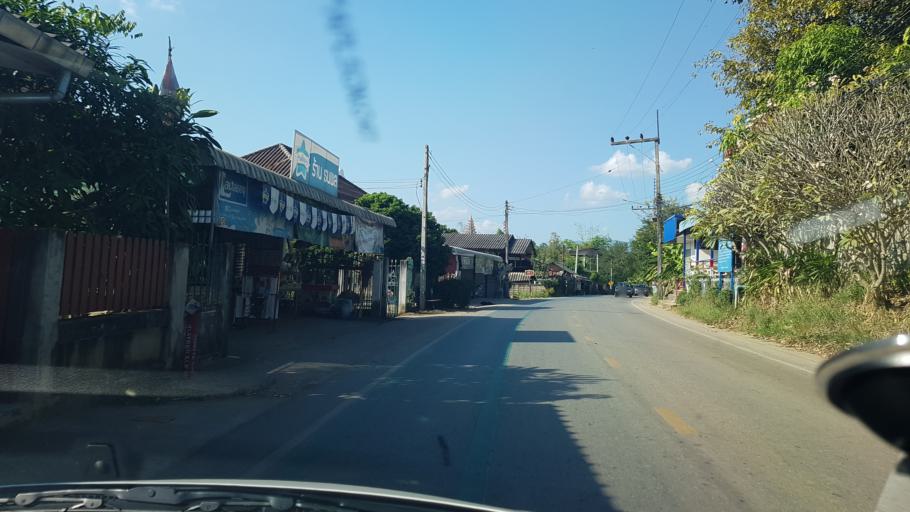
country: TH
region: Chiang Rai
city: Chiang Rai
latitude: 19.9437
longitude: 99.8111
